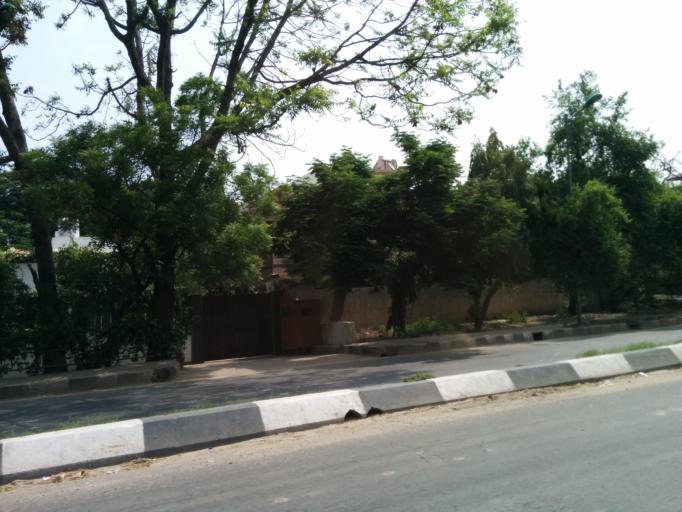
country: IN
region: NCT
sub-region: New Delhi
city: New Delhi
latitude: 28.5455
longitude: 77.1985
